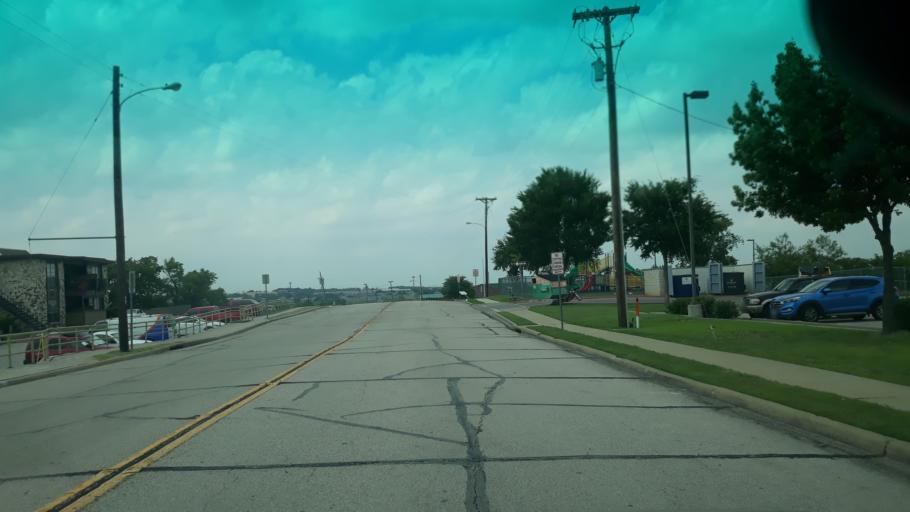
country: US
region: Texas
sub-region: Dallas County
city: Irving
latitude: 32.8574
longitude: -96.9878
